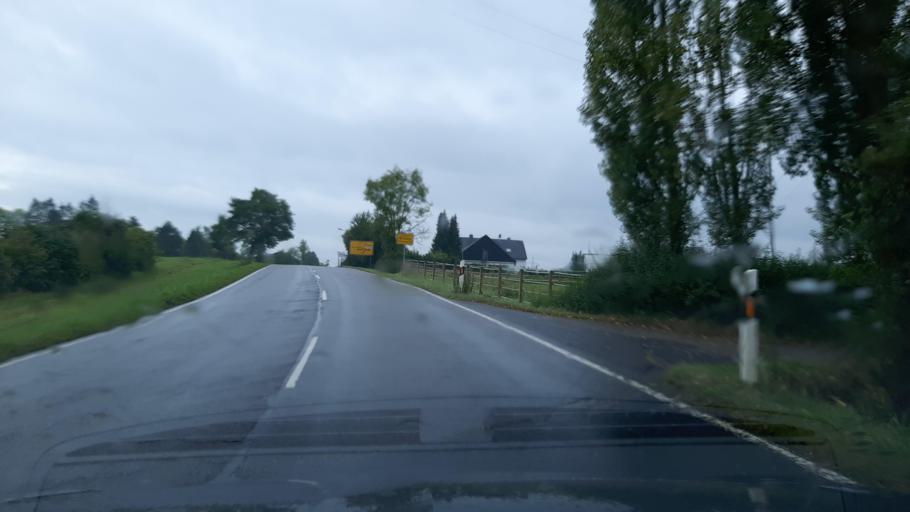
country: DE
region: Rheinland-Pfalz
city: Bitburg
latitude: 49.9658
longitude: 6.5377
